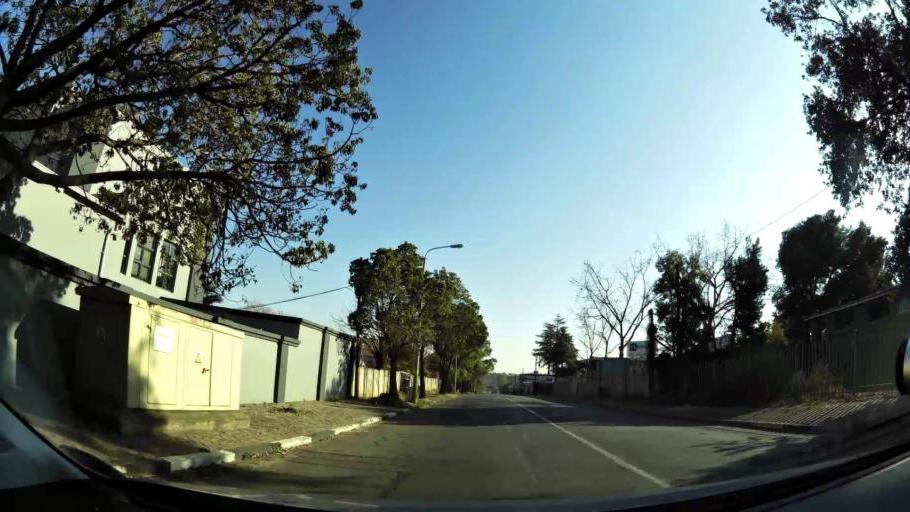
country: ZA
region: Gauteng
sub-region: City of Johannesburg Metropolitan Municipality
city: Modderfontein
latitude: -26.1377
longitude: 28.1643
